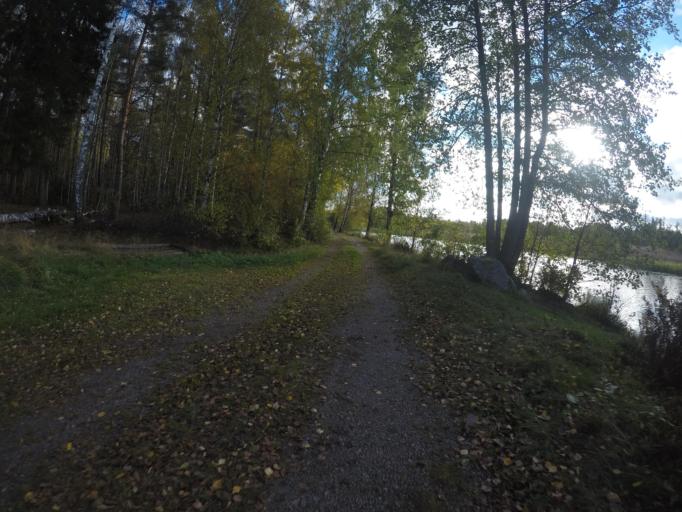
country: SE
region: Vaestmanland
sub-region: Arboga Kommun
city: Tyringe
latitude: 59.3617
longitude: 15.9554
